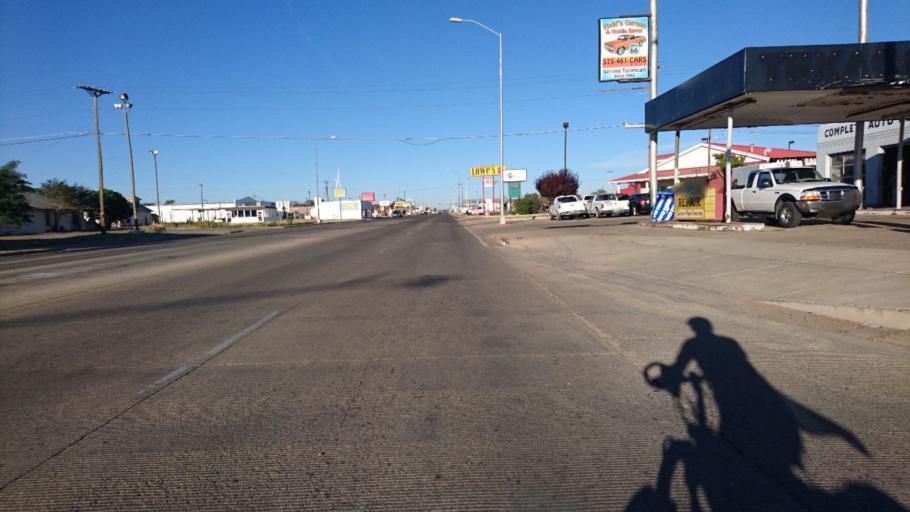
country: US
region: New Mexico
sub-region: Quay County
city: Tucumcari
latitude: 35.1719
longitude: -103.7250
